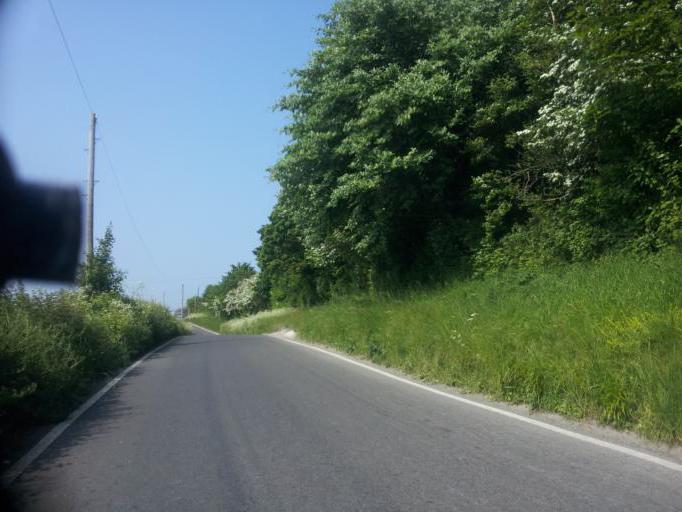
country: GB
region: England
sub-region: Medway
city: Cuxton
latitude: 51.3568
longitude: 0.4735
